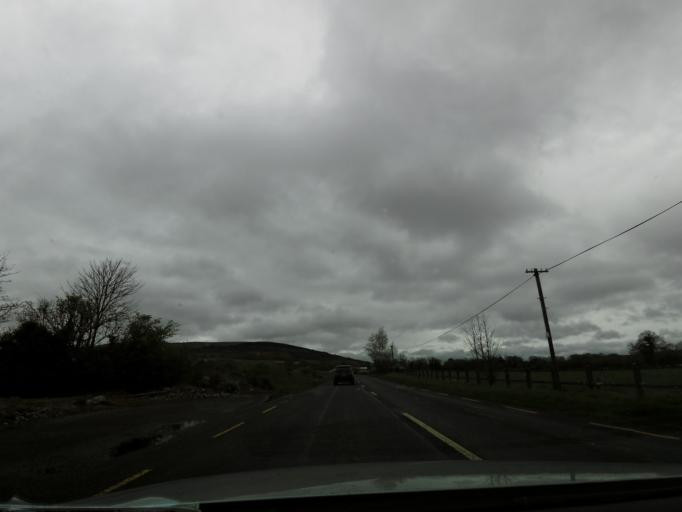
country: IE
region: Leinster
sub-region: Laois
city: Rathdowney
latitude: 52.7197
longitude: -7.5321
